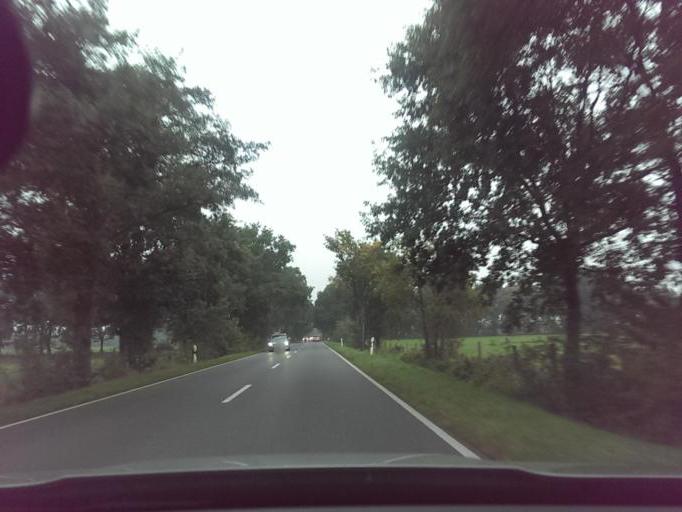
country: DE
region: Lower Saxony
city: Garbsen-Mitte
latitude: 52.4634
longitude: 9.6451
